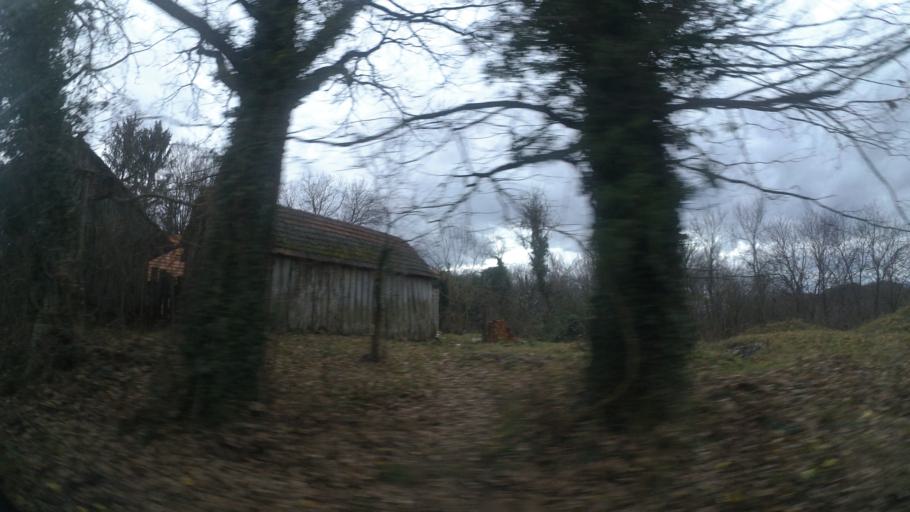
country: HR
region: Karlovacka
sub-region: Grad Karlovac
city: Karlovac
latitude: 45.3894
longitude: 15.5383
